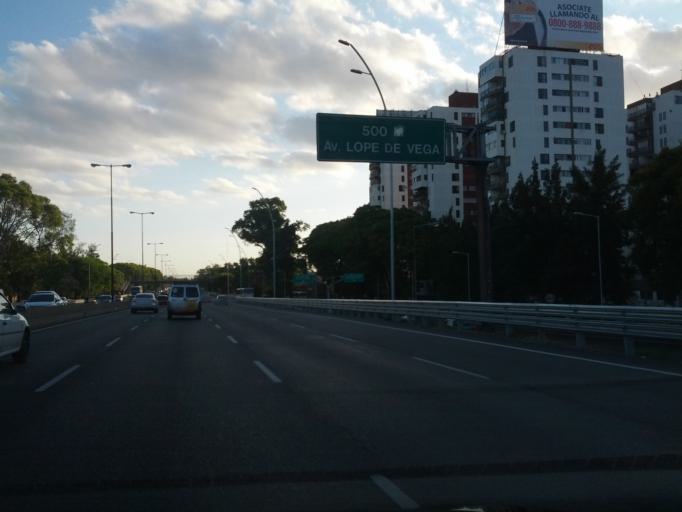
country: AR
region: Buenos Aires
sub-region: Partido de General San Martin
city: General San Martin
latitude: -34.6041
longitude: -58.5257
